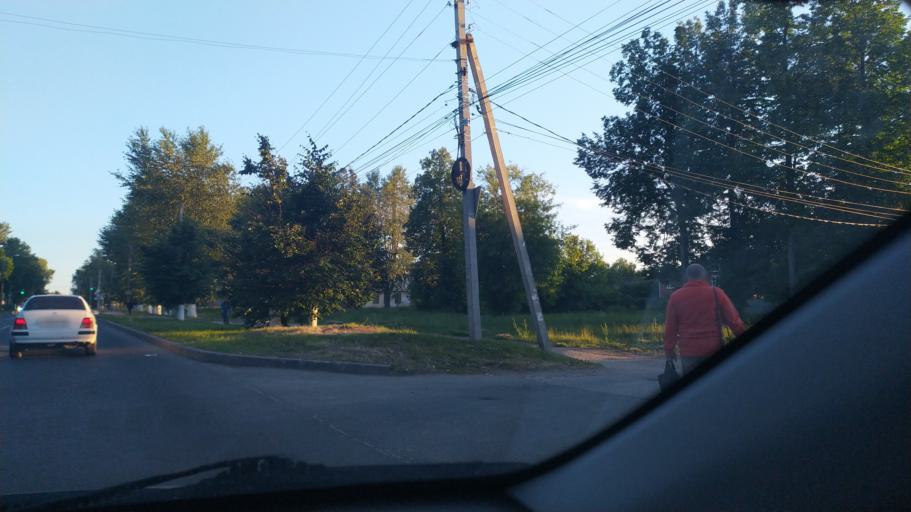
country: RU
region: Chuvashia
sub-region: Cheboksarskiy Rayon
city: Cheboksary
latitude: 56.1221
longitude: 47.2269
